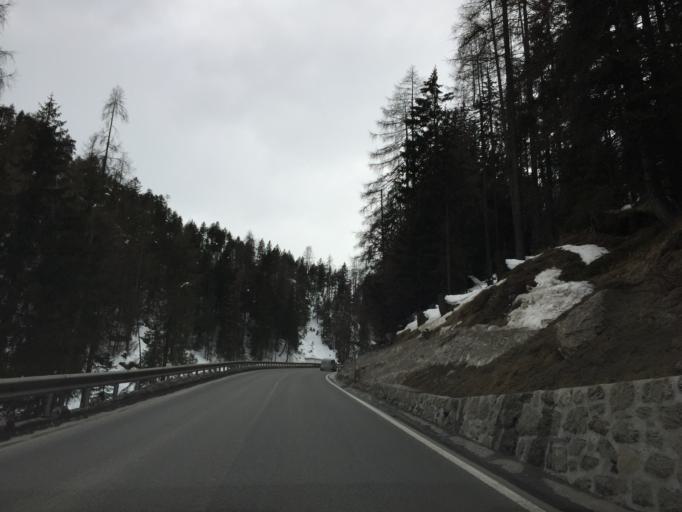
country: CH
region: Grisons
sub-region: Praettigau/Davos District
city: Davos
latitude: 46.8406
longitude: 9.8643
